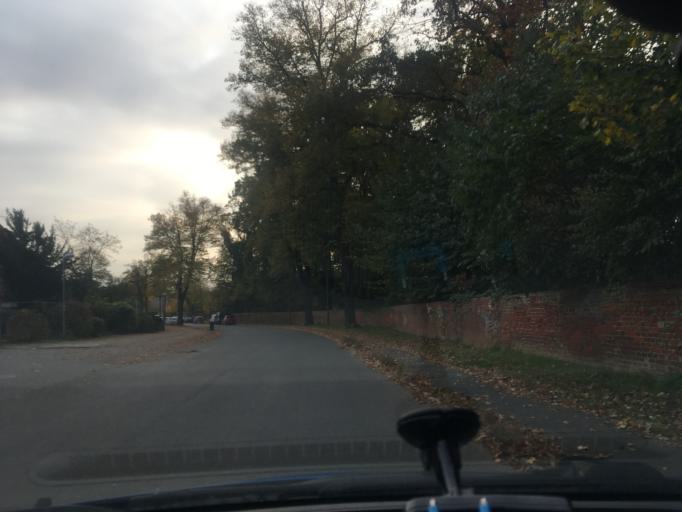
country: DE
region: Lower Saxony
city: Lueneburg
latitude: 53.2591
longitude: 10.4226
